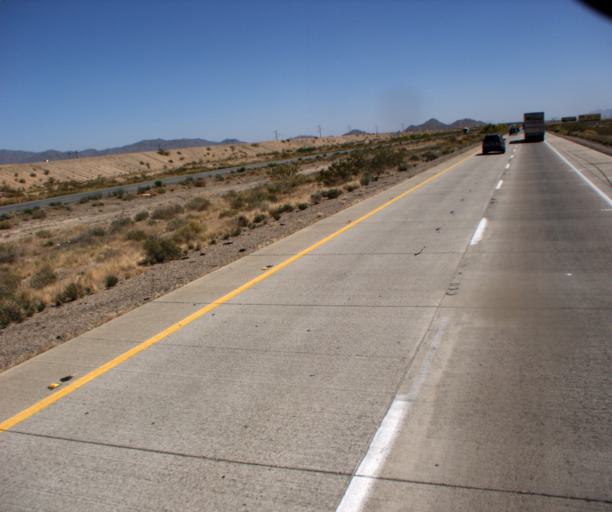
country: US
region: Arizona
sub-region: Maricopa County
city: Buckeye
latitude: 33.4426
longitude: -112.6932
